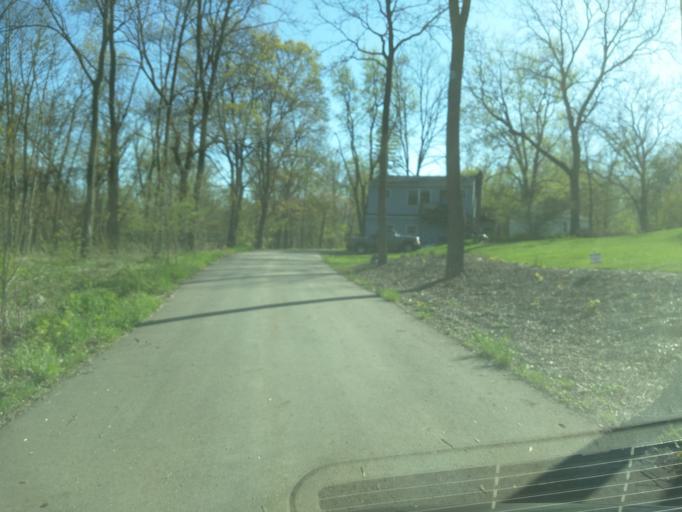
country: US
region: Michigan
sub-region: Eaton County
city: Waverly
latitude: 42.7627
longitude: -84.6481
